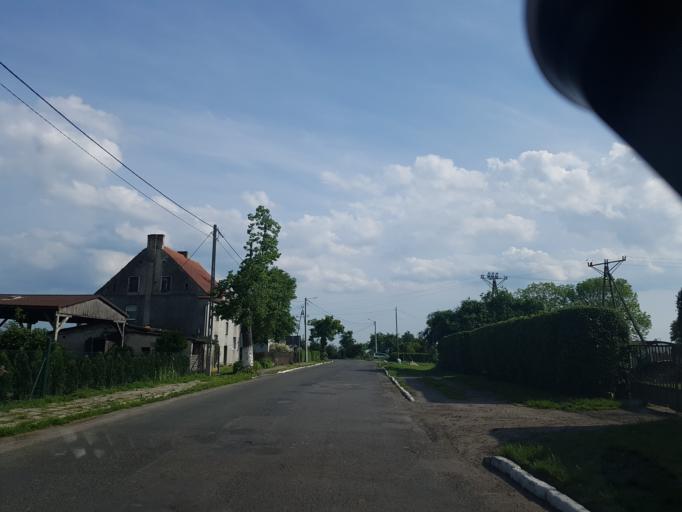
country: PL
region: Lower Silesian Voivodeship
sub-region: Powiat olawski
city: Wierzbno
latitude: 50.9087
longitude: 17.1246
